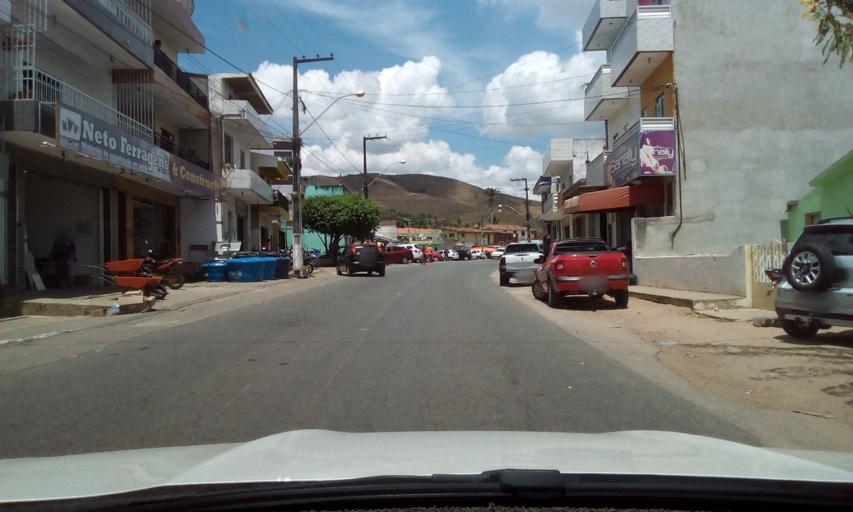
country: BR
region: Paraiba
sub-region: Alagoinha
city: Alagoinha
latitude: -6.9505
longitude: -35.5451
